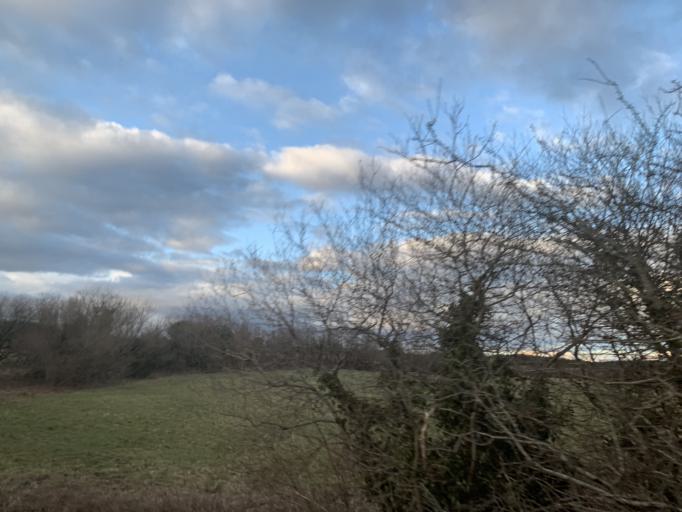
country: IE
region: Connaught
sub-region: Maigh Eo
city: Ballyhaunis
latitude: 53.8640
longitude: -8.7560
